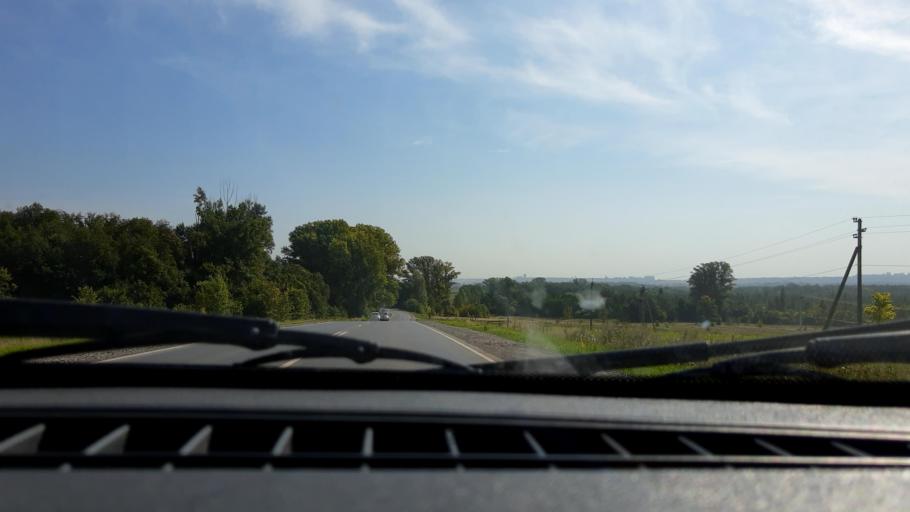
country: RU
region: Bashkortostan
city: Mikhaylovka
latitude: 54.8322
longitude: 55.9267
